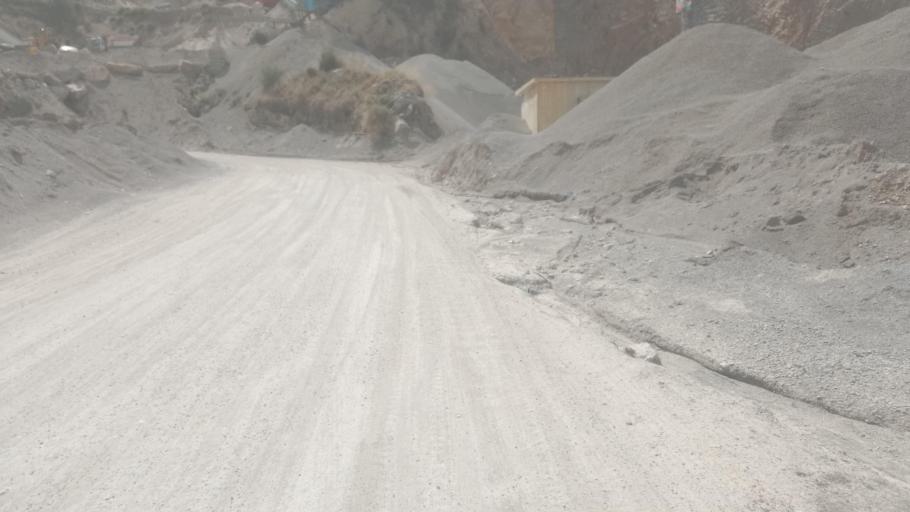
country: PK
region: Khyber Pakhtunkhwa
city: Abbottabad
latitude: 34.1615
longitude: 73.2810
